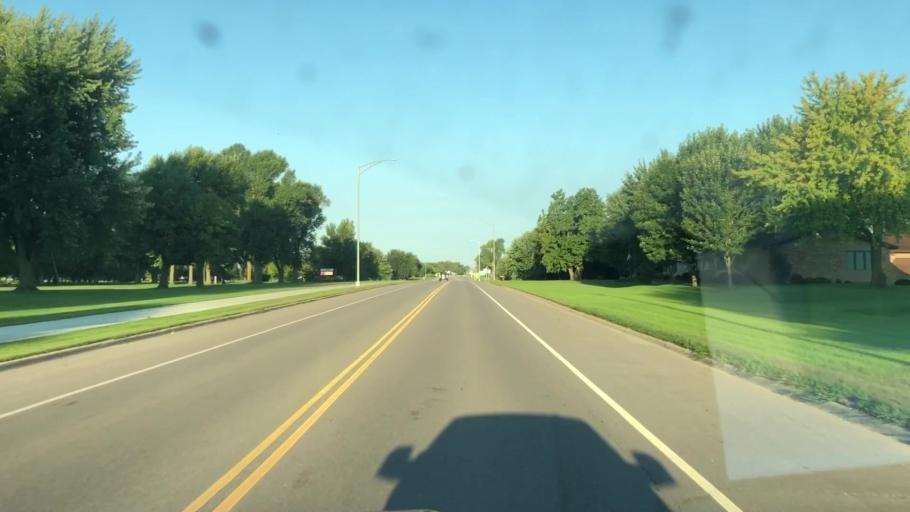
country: US
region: Minnesota
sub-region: Nobles County
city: Worthington
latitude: 43.6310
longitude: -95.6214
